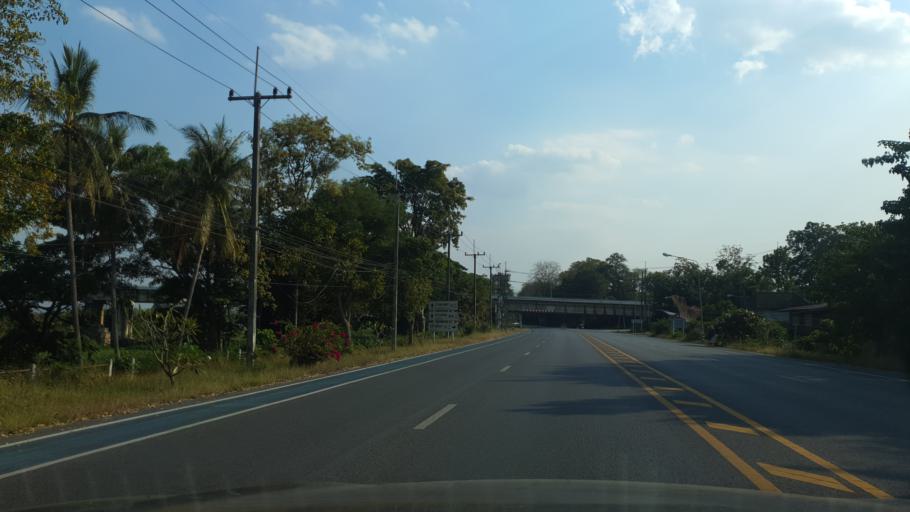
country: TH
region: Tak
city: Tak
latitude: 16.8572
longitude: 99.1220
